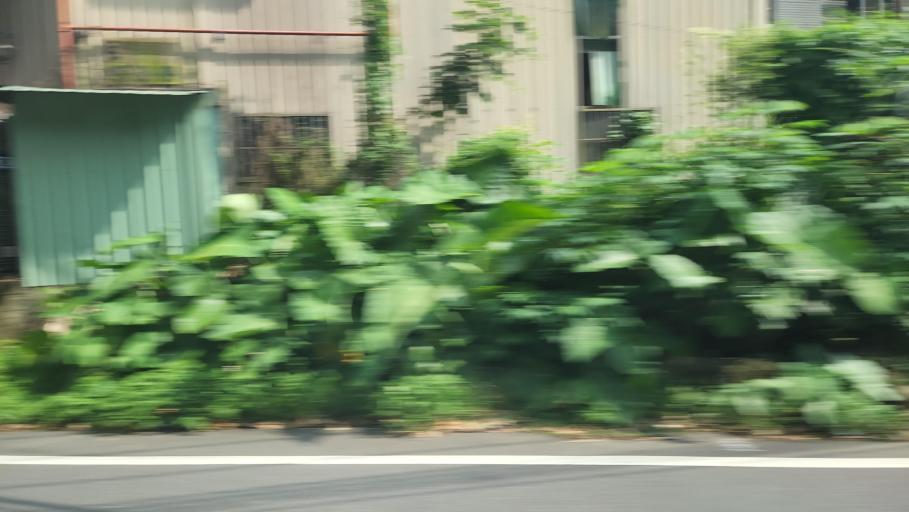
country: TW
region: Taiwan
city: Daxi
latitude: 24.9125
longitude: 121.3737
